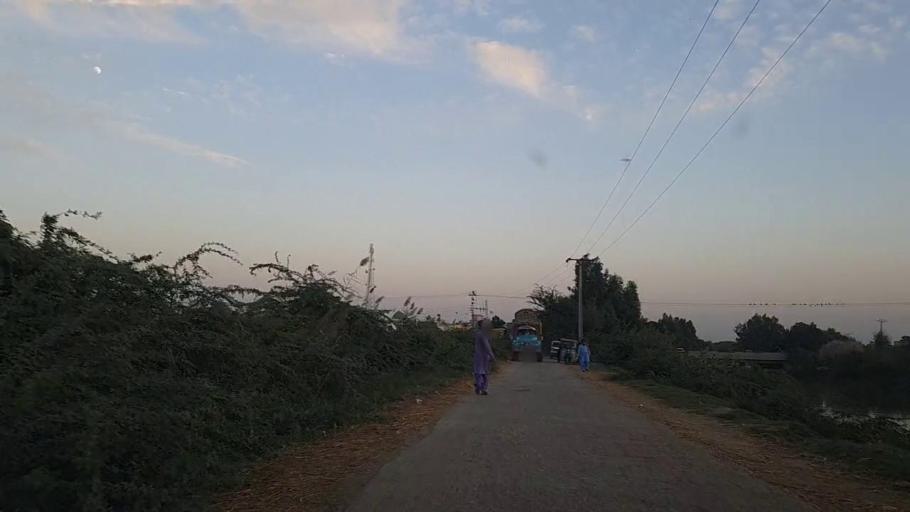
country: PK
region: Sindh
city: Thatta
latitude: 24.7942
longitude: 67.9565
